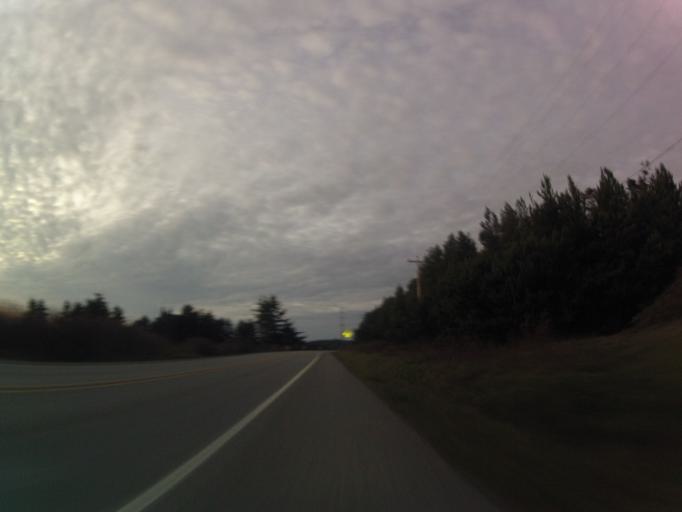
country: US
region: Washington
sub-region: Island County
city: Coupeville
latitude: 48.1781
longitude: -122.6865
